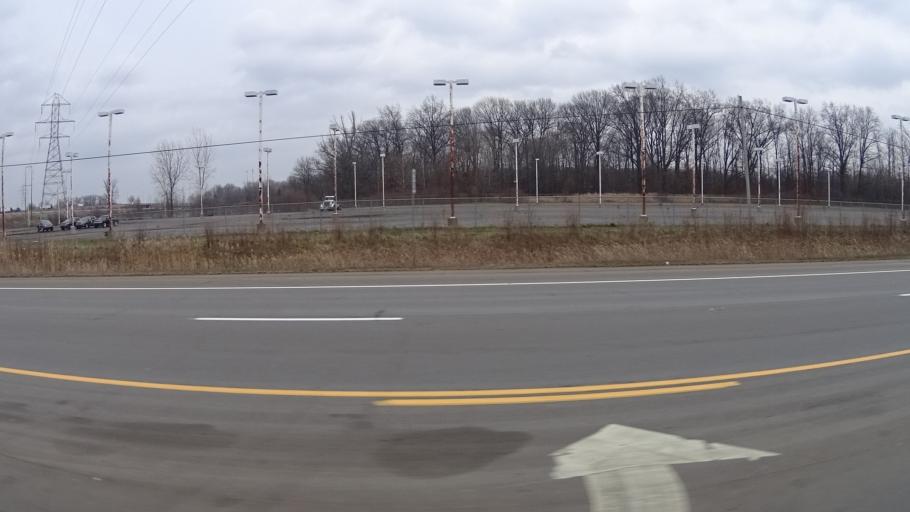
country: US
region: Ohio
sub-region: Lorain County
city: Amherst
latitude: 41.3785
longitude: -82.2103
